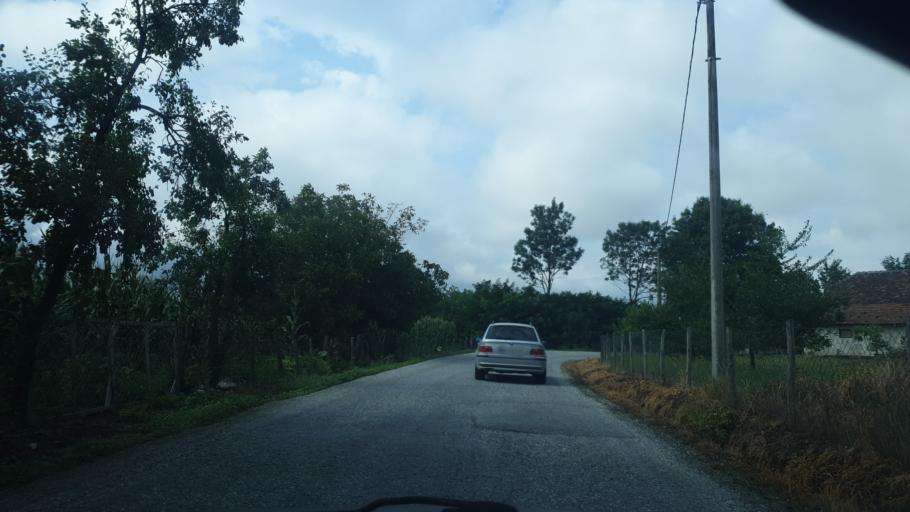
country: RS
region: Central Serbia
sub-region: Sumadijski Okrug
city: Kragujevac
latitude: 44.1079
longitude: 20.8101
